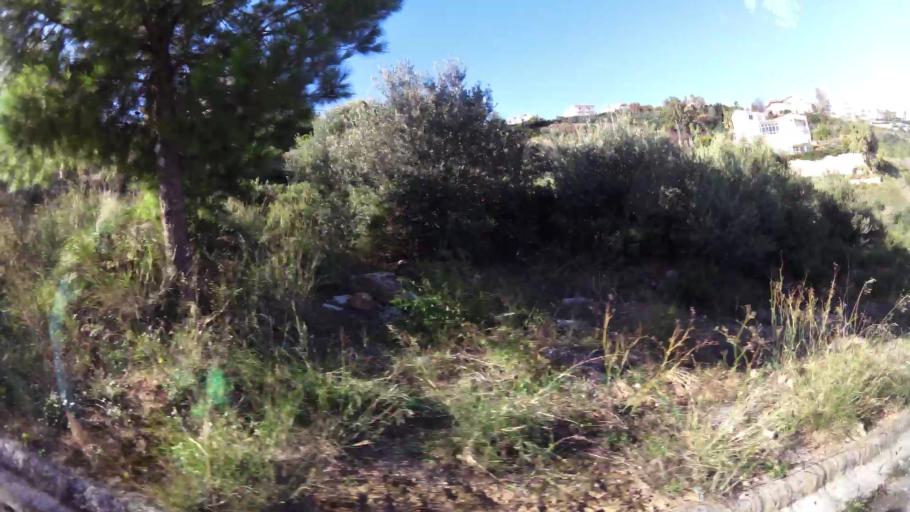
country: GR
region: Attica
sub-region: Nomarchia Anatolikis Attikis
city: Dhrafi
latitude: 38.0252
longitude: 23.9048
